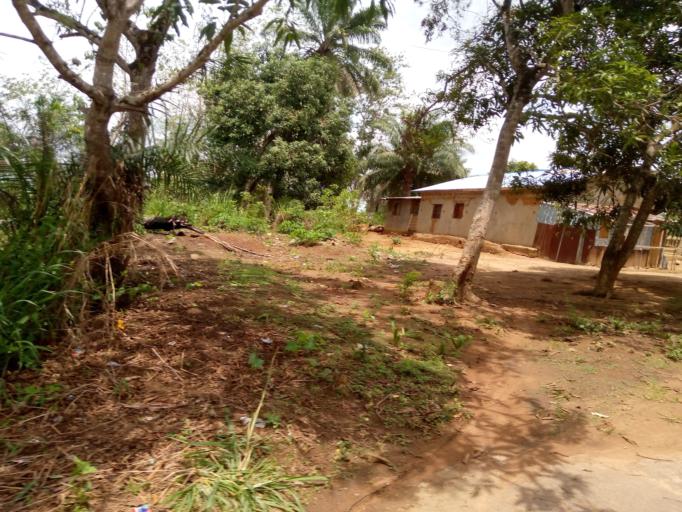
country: SL
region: Western Area
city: Waterloo
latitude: 8.3426
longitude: -12.9855
